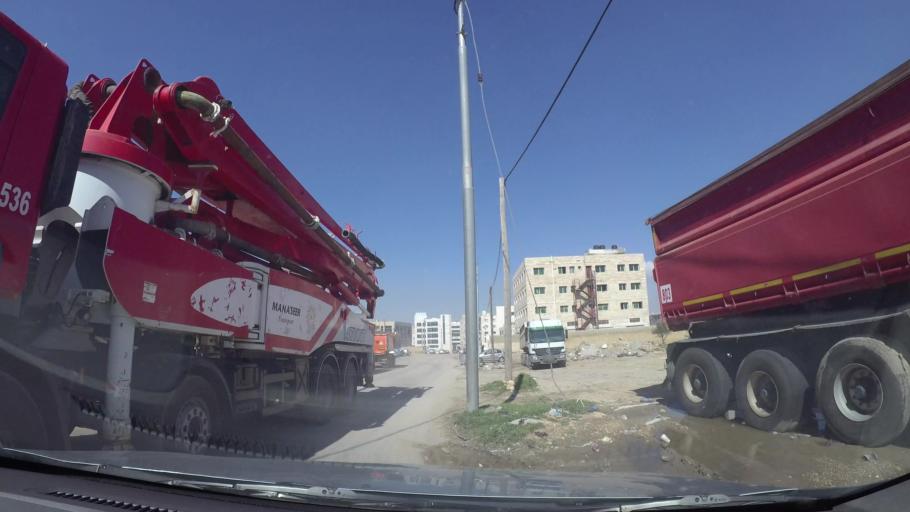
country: JO
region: Amman
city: Al Bunayyat ash Shamaliyah
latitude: 31.9122
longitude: 35.9134
